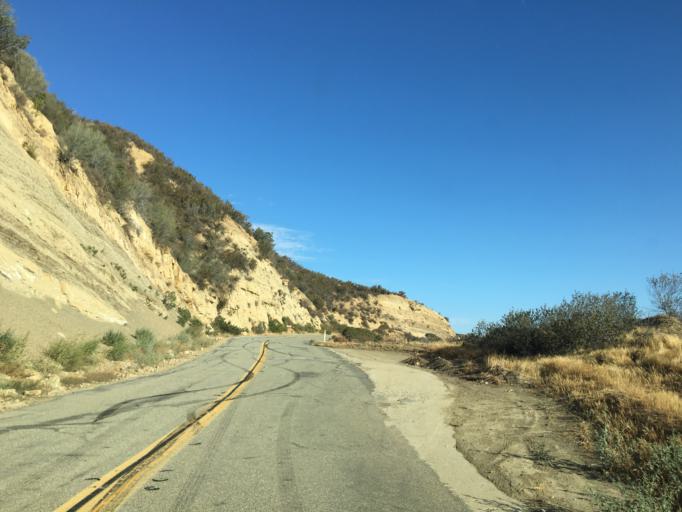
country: US
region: California
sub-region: Los Angeles County
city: Castaic
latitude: 34.5742
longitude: -118.6681
